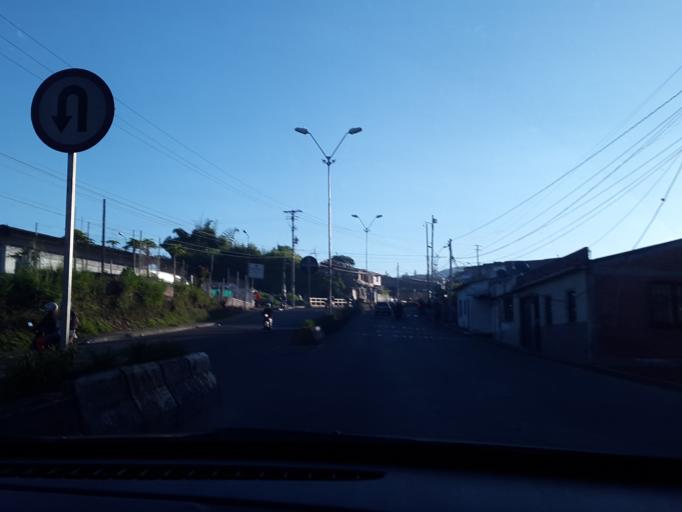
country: CO
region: Quindio
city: Armenia
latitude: 4.5316
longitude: -75.6880
